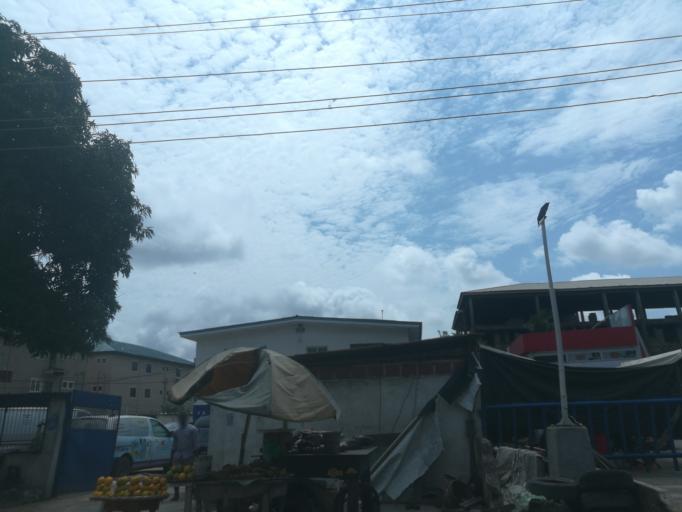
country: NG
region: Lagos
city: Somolu
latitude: 6.5252
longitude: 3.3814
